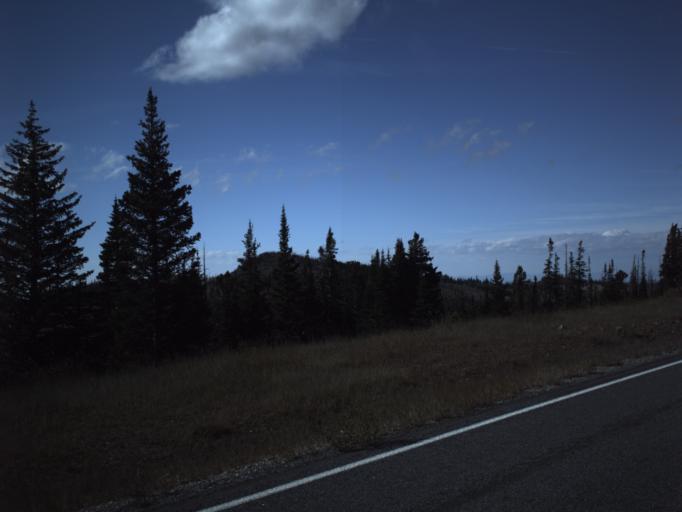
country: US
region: Utah
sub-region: Iron County
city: Parowan
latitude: 37.6726
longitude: -112.8412
